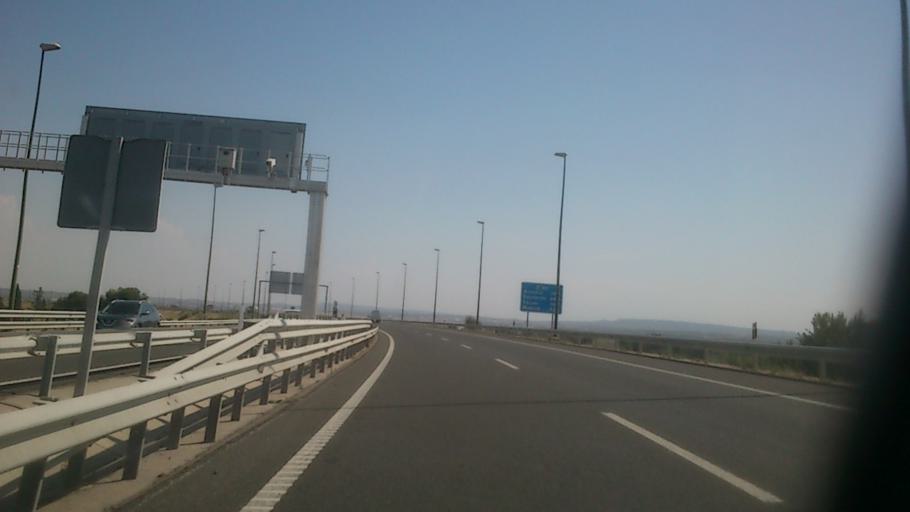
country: ES
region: Aragon
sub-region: Provincia de Zaragoza
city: Zaragoza
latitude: 41.6573
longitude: -0.8411
